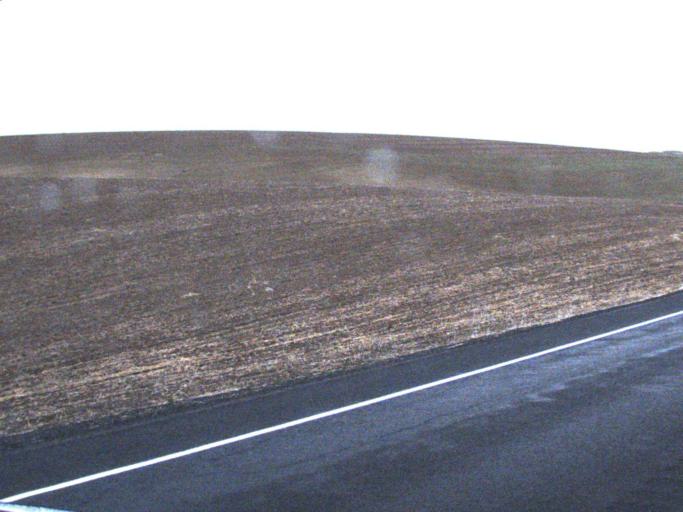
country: US
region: Washington
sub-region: Whitman County
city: Colfax
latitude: 46.8287
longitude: -117.5188
